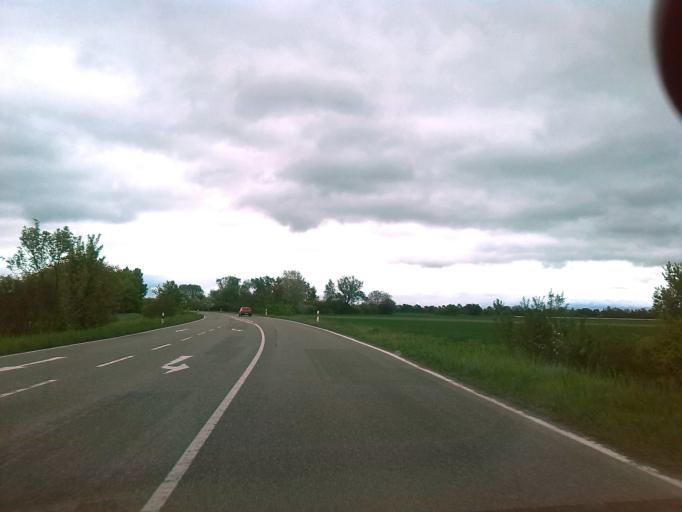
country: DE
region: Rheinland-Pfalz
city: Bohl-Iggelheim
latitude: 49.3773
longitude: 8.3272
